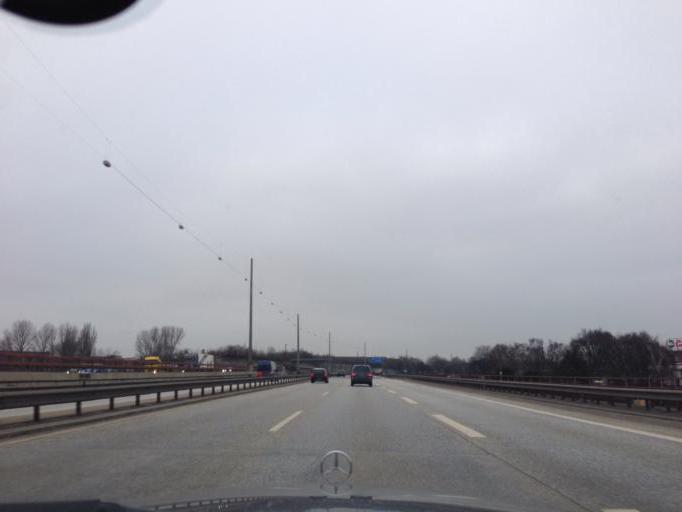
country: DE
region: Hamburg
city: Rothenburgsort
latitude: 53.5217
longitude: 10.0253
